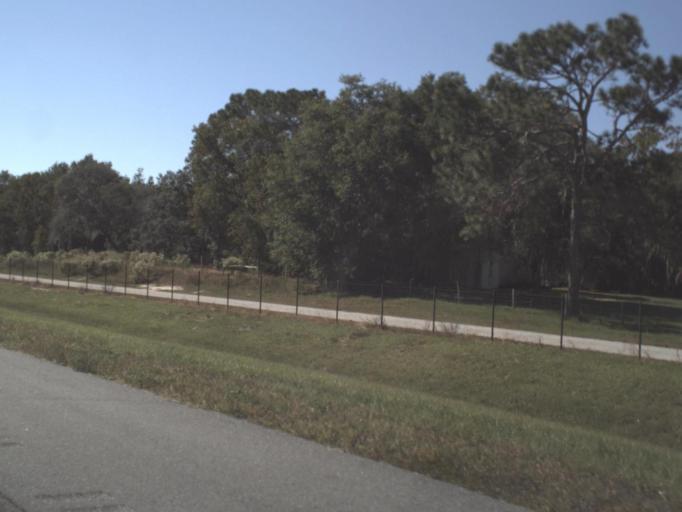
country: US
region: Florida
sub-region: Pasco County
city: Shady Hills
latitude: 28.3823
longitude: -82.5397
